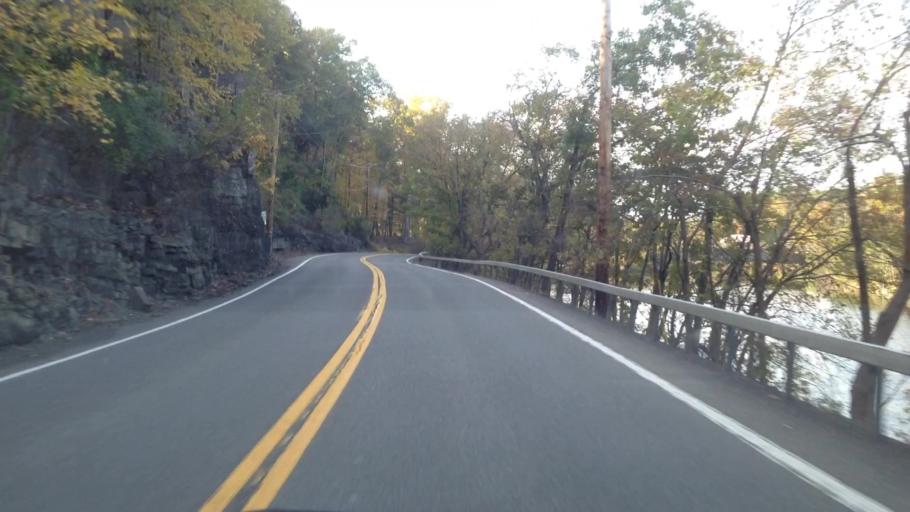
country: US
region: New York
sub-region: Ulster County
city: Tillson
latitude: 41.8196
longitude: -74.0526
